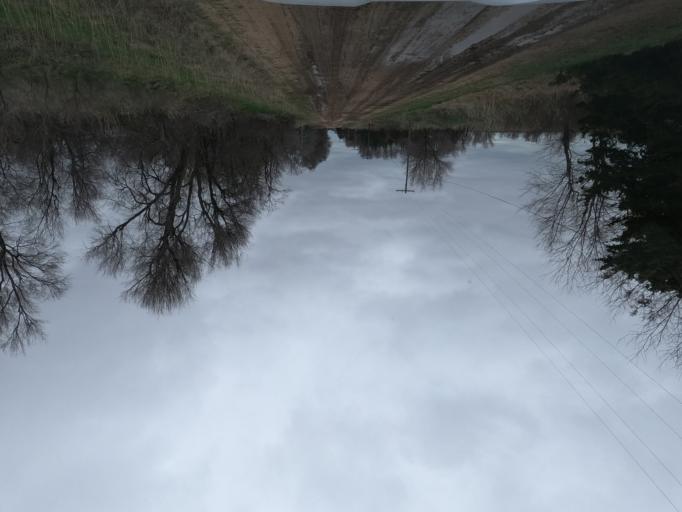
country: US
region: Kansas
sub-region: Rice County
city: Sterling
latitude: 37.9737
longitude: -98.3072
